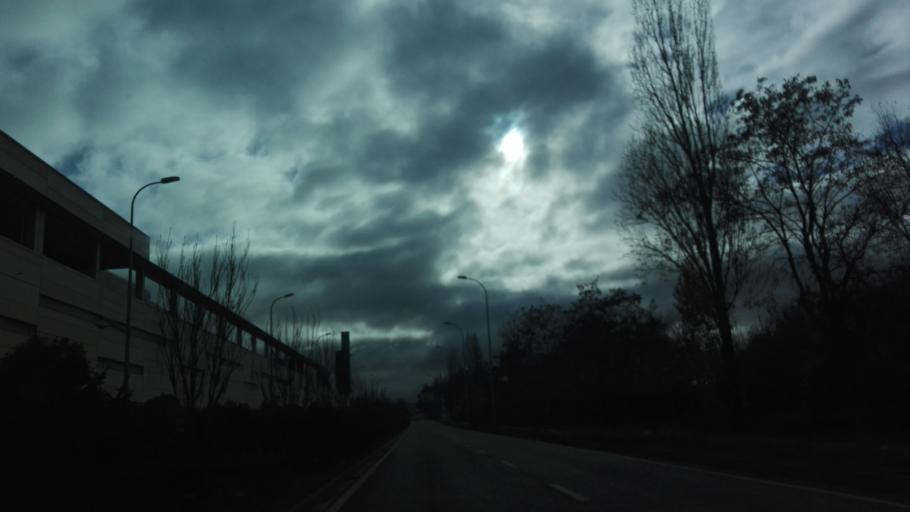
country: ES
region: Navarre
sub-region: Provincia de Navarra
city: Egues-Uharte
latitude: 42.8291
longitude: -1.5848
